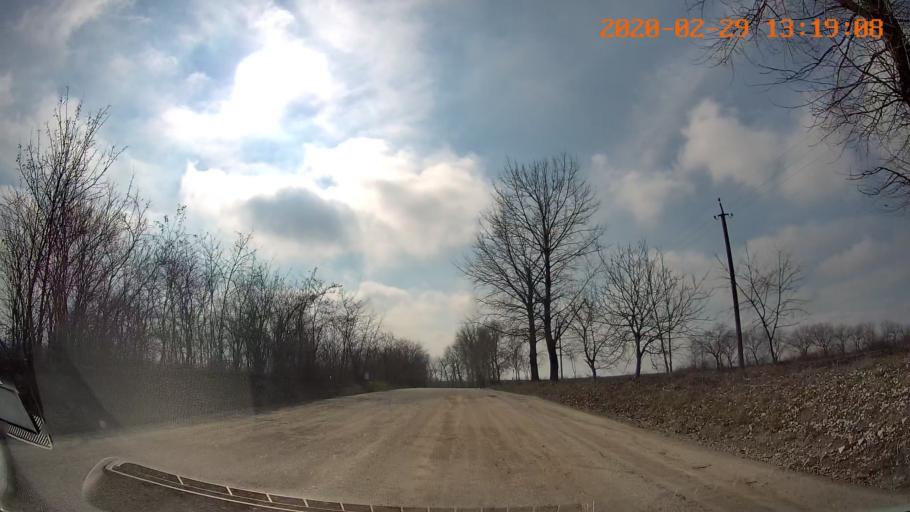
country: MD
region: Telenesti
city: Camenca
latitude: 47.9909
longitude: 28.6534
